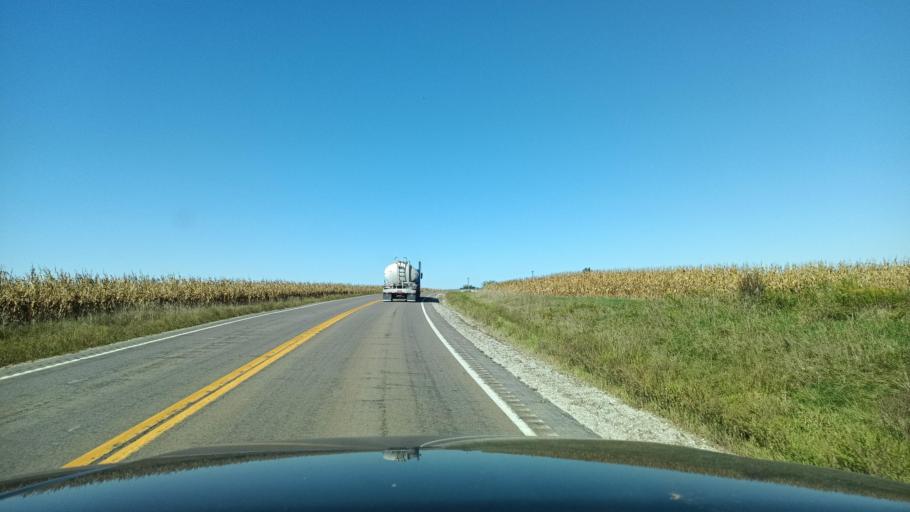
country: US
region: Missouri
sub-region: Scotland County
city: Memphis
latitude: 40.4507
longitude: -92.1023
